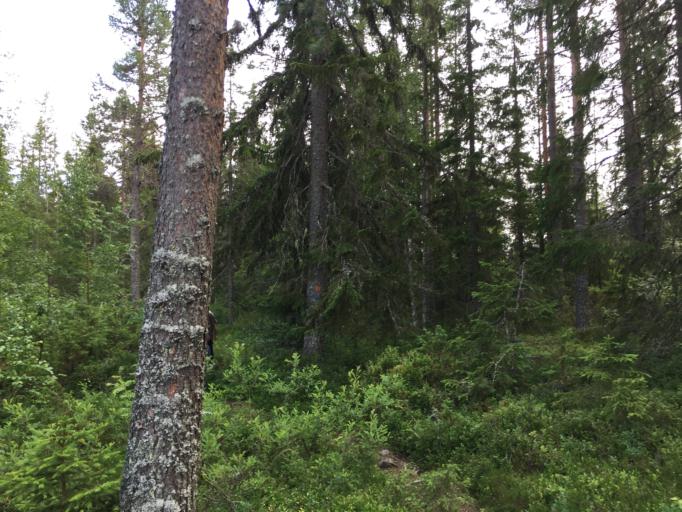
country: SE
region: Dalarna
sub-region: Malung-Saelens kommun
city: Malung
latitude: 60.6410
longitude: 13.7735
